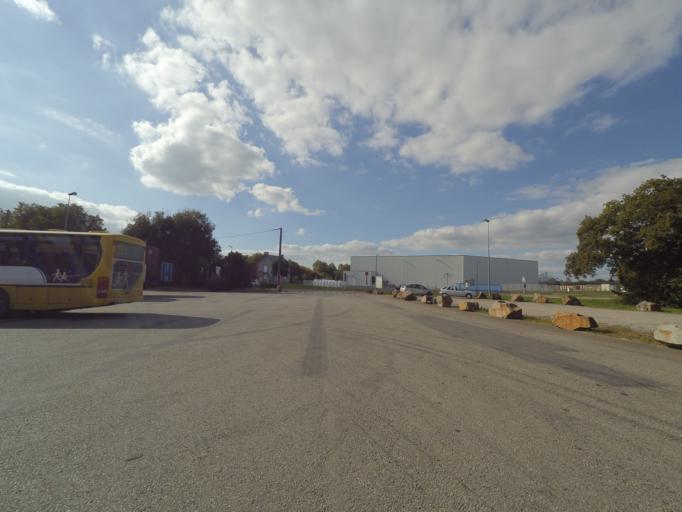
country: FR
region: Pays de la Loire
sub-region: Departement de la Loire-Atlantique
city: Chemere
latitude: 47.1248
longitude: -1.9098
